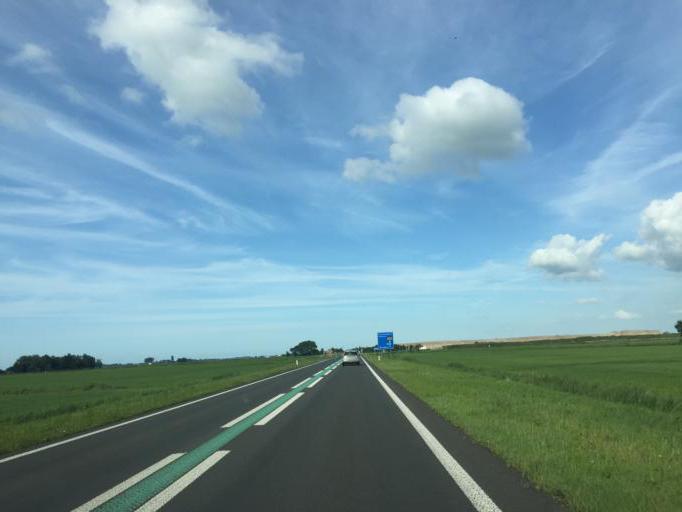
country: NL
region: Friesland
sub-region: Gemeente Ferwerderadiel
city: Burdaard
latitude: 53.2788
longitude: 5.8988
